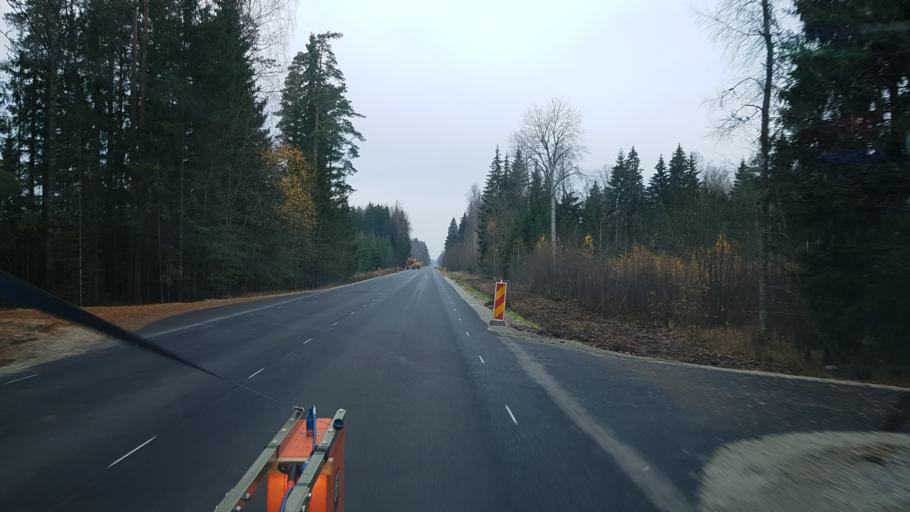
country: EE
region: Paernumaa
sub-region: Vaendra vald (alev)
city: Vandra
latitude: 58.8297
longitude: 25.1069
